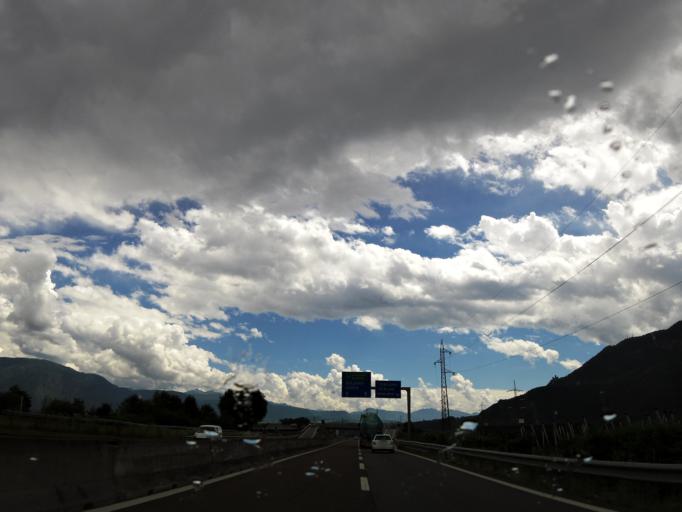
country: IT
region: Trentino-Alto Adige
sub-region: Bolzano
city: Terlano
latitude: 46.5248
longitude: 11.2433
